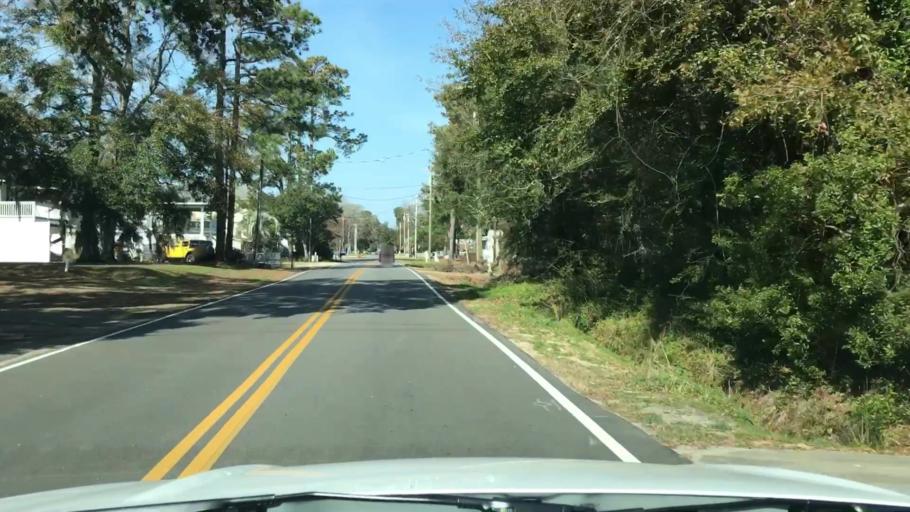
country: US
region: South Carolina
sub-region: Horry County
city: Garden City
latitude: 33.5886
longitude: -78.9948
